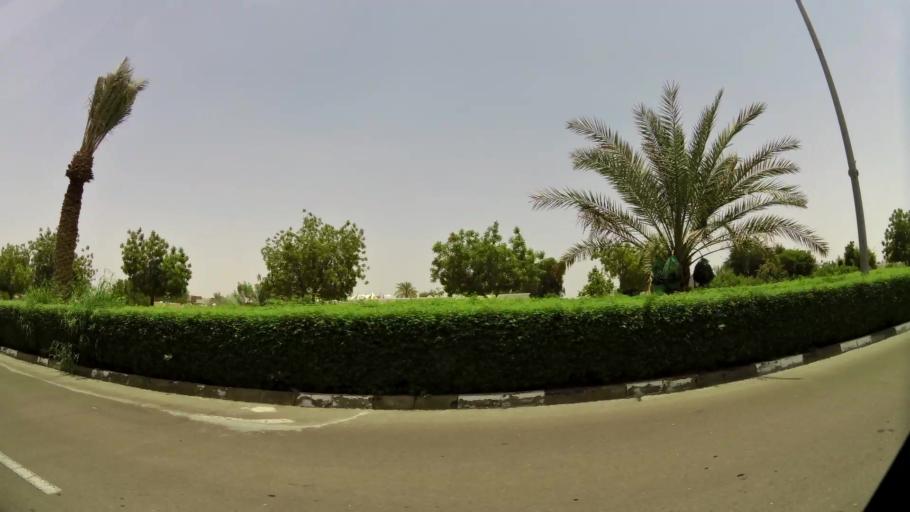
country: AE
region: Abu Dhabi
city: Al Ain
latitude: 24.2186
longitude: 55.7328
